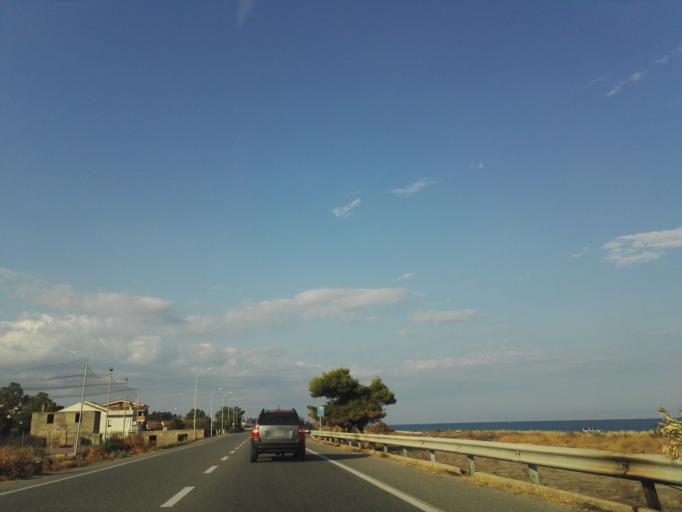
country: IT
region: Calabria
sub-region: Provincia di Reggio Calabria
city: Riace Marina
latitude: 38.3842
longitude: 16.5231
